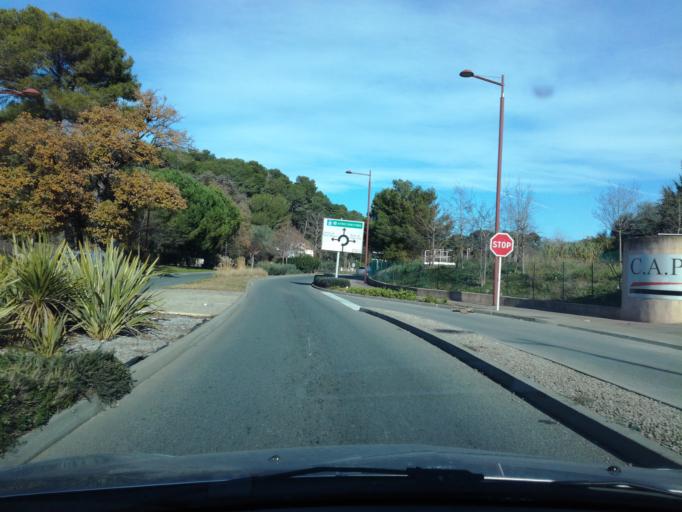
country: FR
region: Provence-Alpes-Cote d'Azur
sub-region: Departement des Alpes-Maritimes
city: Vallauris
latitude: 43.5844
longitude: 7.0901
